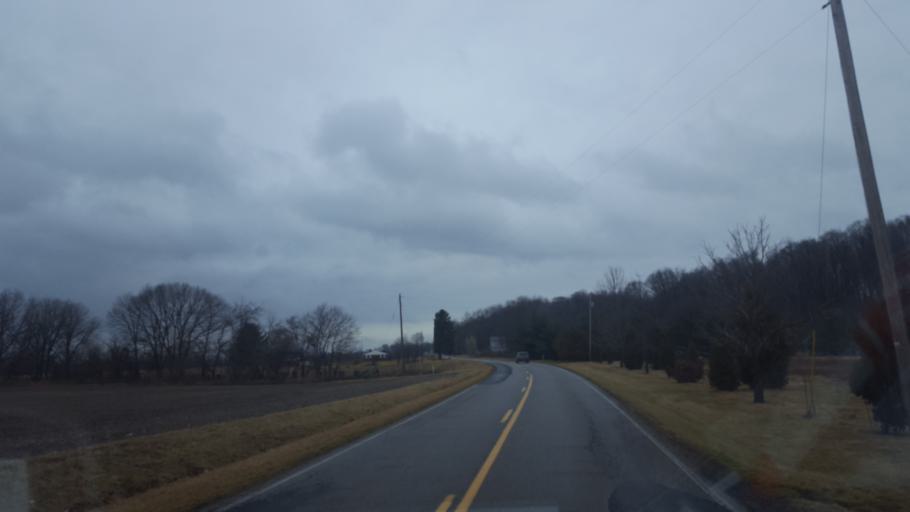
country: US
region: Ohio
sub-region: Knox County
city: Fredericktown
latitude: 40.4474
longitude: -82.5118
